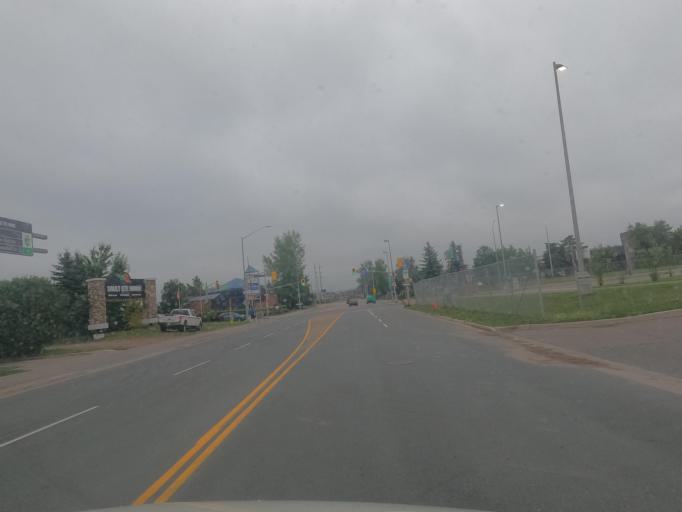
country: CA
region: Ontario
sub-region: Algoma
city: Sault Ste. Marie
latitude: 46.5190
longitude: -84.3478
